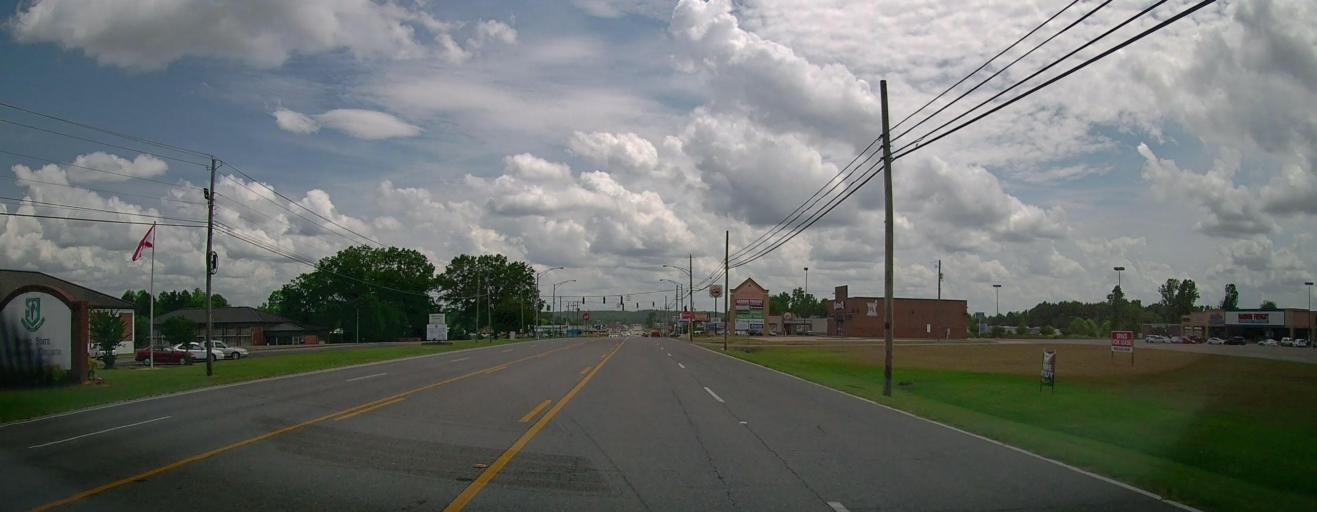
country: US
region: Alabama
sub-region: Marion County
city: Hamilton
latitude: 34.1235
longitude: -87.9898
